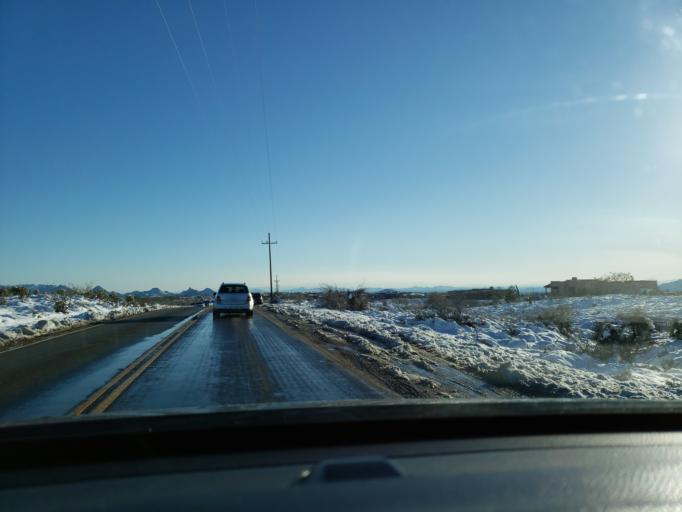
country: US
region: Arizona
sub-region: Maricopa County
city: Carefree
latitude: 33.8624
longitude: -111.8297
